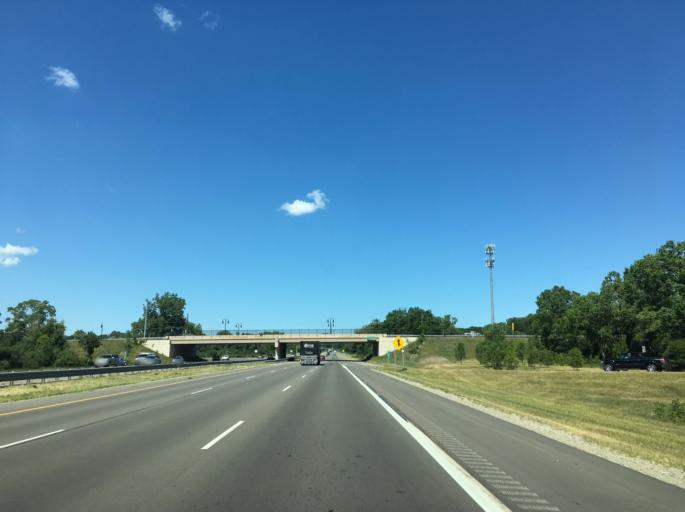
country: US
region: Michigan
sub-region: Oakland County
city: Clarkston
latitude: 42.7465
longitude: -83.4172
